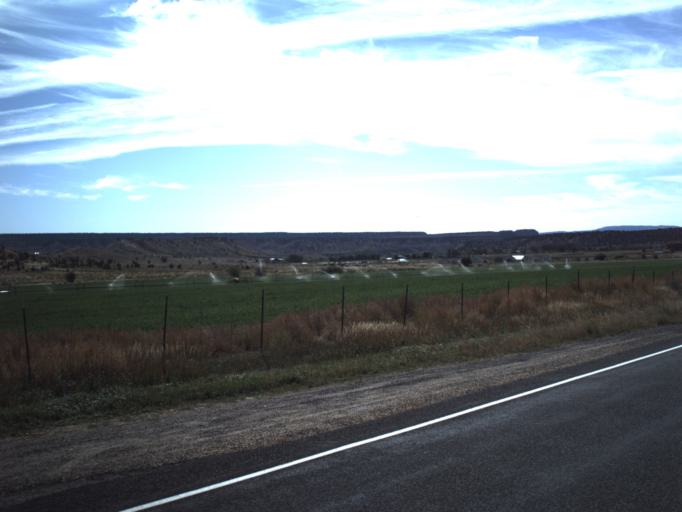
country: US
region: Utah
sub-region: Garfield County
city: Panguitch
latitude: 37.6379
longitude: -112.0819
